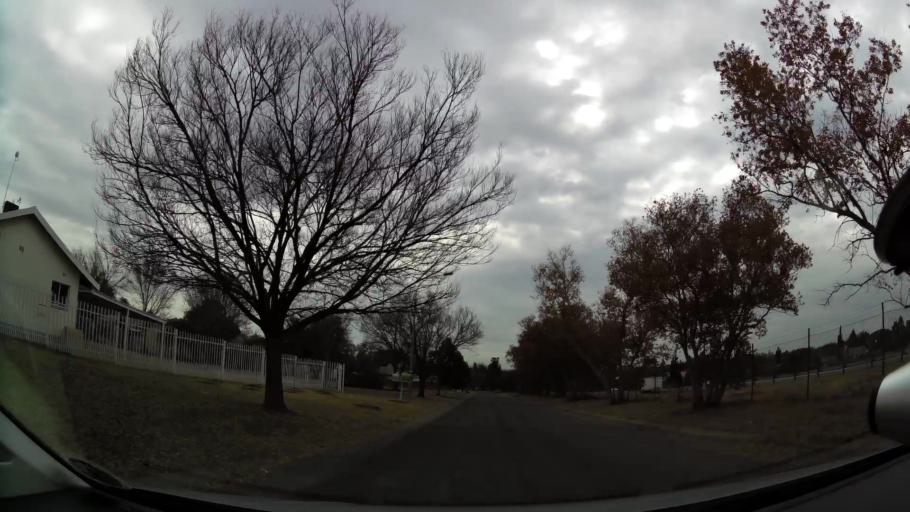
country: ZA
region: Orange Free State
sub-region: Fezile Dabi District Municipality
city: Kroonstad
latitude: -27.6842
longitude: 27.2403
